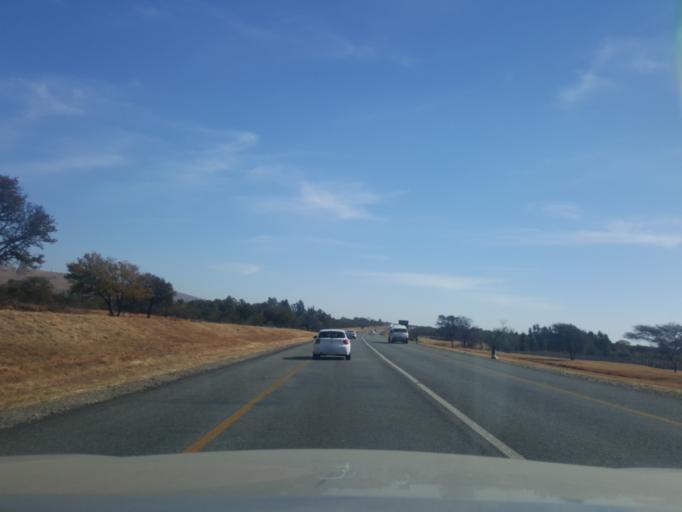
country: ZA
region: North-West
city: Ga-Rankuwa
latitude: -25.6569
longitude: 28.0302
